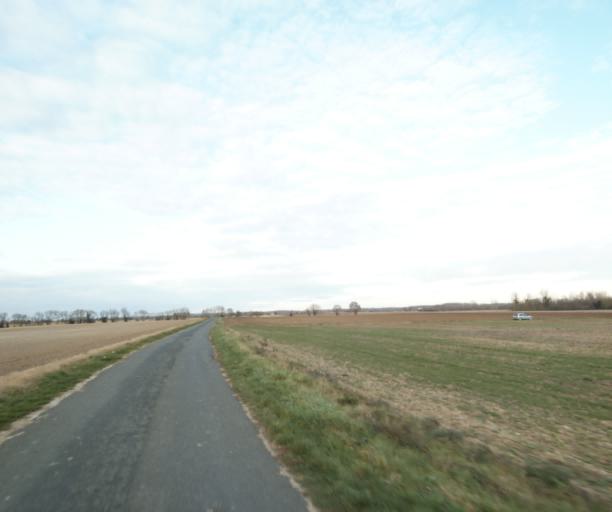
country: FR
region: Poitou-Charentes
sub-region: Departement de la Charente-Maritime
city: Les Gonds
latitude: 45.6999
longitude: -0.6178
